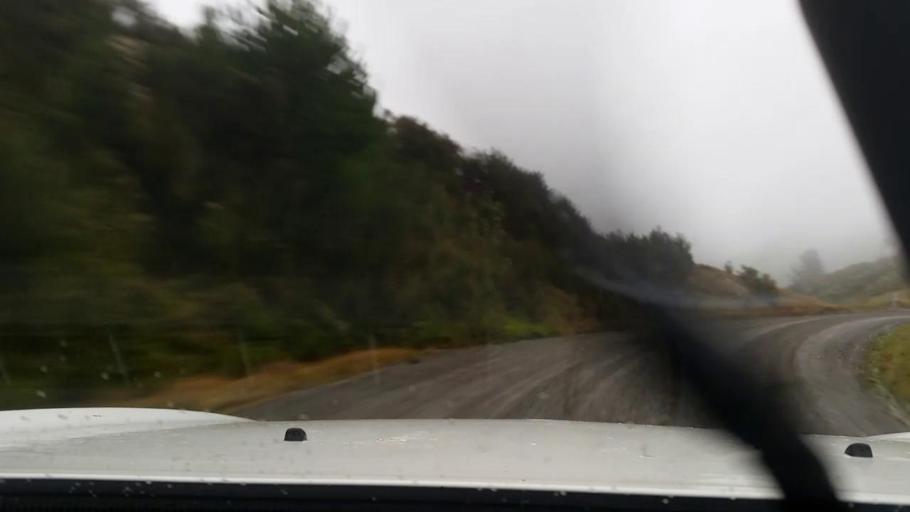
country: NZ
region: Wellington
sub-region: Masterton District
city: Masterton
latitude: -41.2474
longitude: 175.8787
